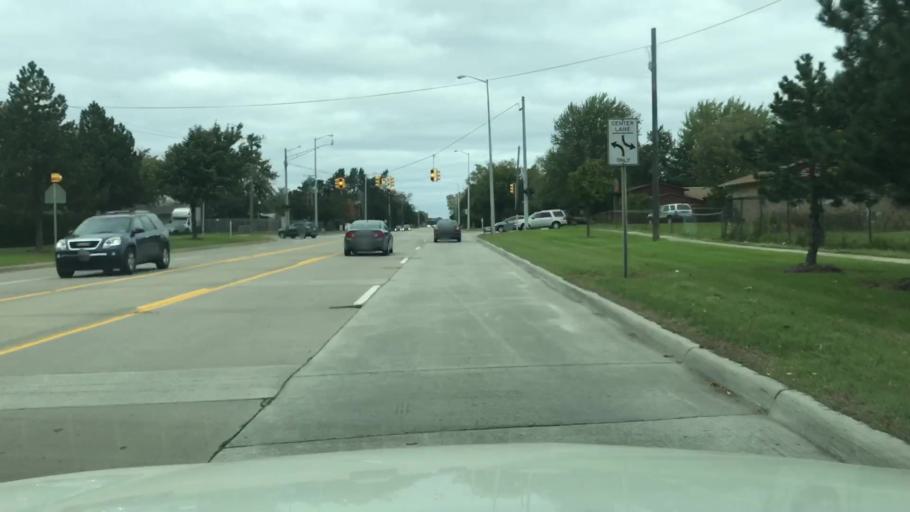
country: US
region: Michigan
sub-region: Macomb County
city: Sterling Heights
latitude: 42.5576
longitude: -83.0695
